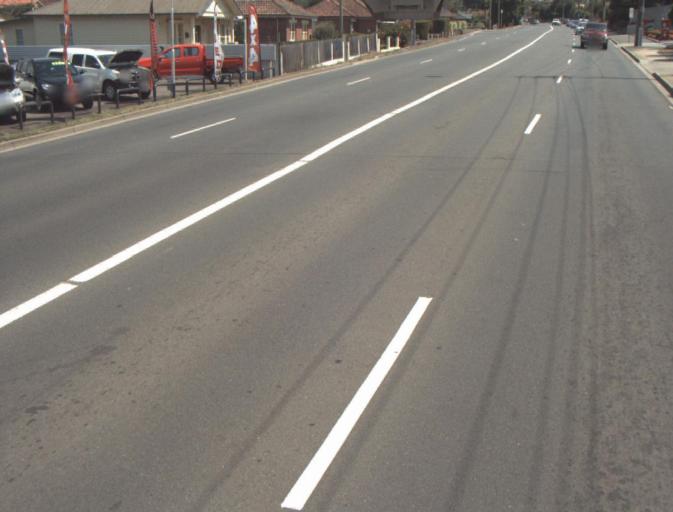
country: AU
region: Tasmania
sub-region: Launceston
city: East Launceston
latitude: -41.4644
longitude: 147.1586
